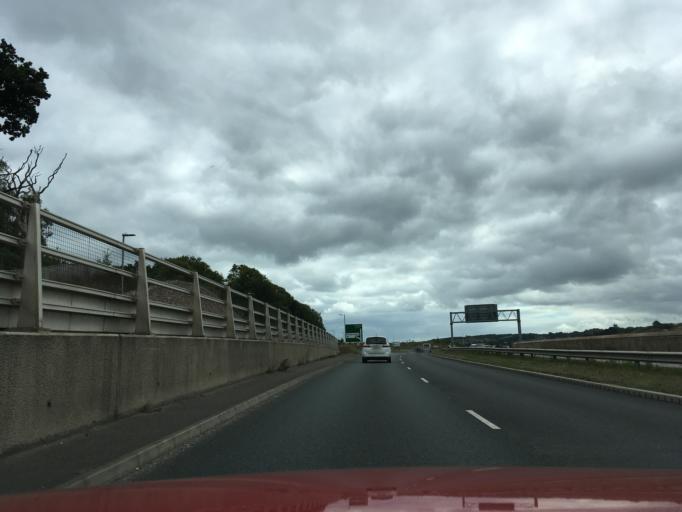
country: GB
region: England
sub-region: Devon
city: Kingskerswell
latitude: 50.5153
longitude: -3.5882
